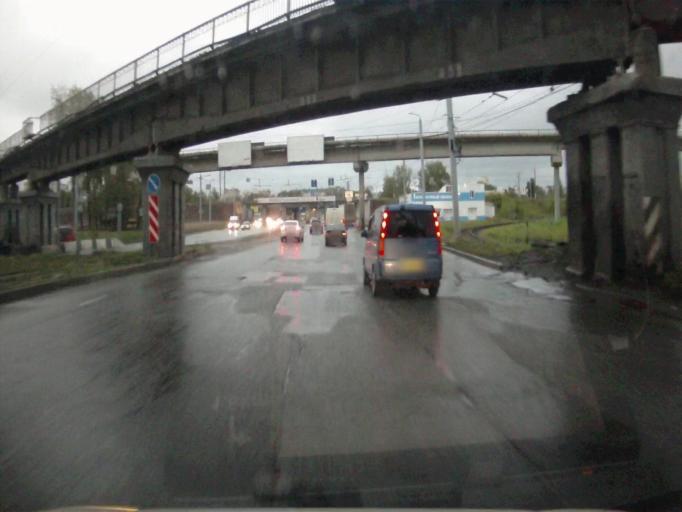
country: RU
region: Chelyabinsk
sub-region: Gorod Chelyabinsk
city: Chelyabinsk
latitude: 55.1540
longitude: 61.4430
